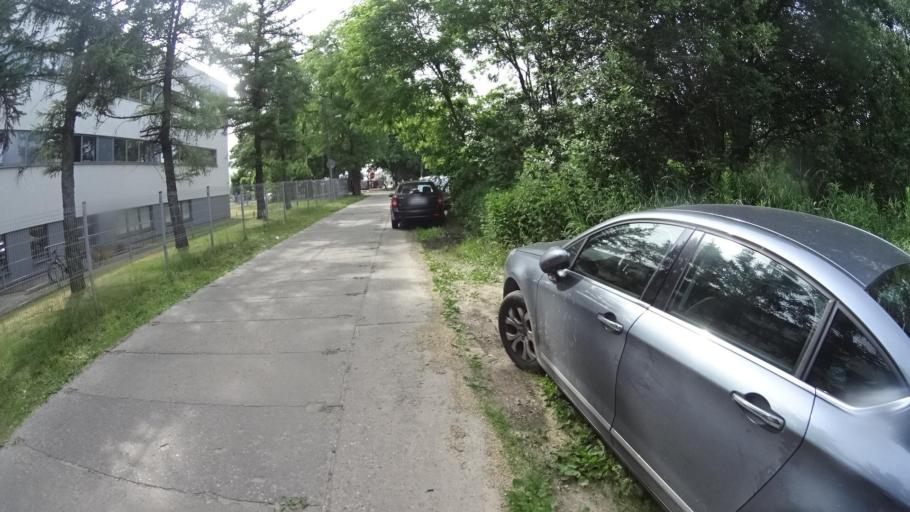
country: PL
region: Masovian Voivodeship
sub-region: Warszawa
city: Wlochy
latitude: 52.1865
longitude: 20.9261
